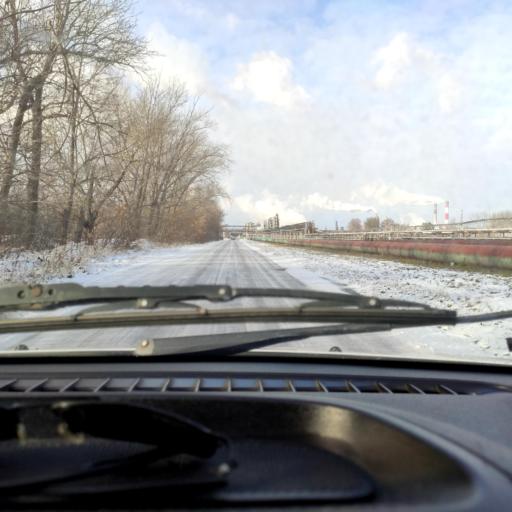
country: RU
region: Samara
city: Tol'yatti
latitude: 53.5347
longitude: 49.4781
